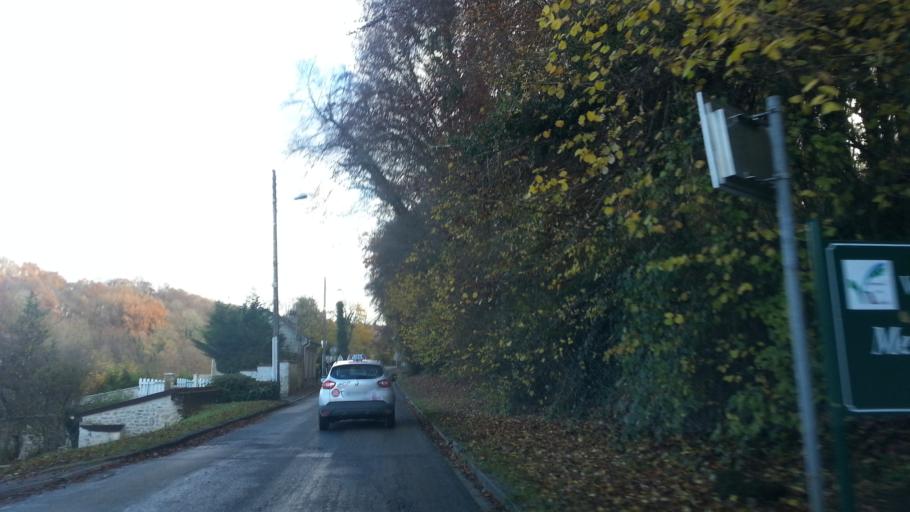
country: FR
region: Picardie
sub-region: Departement de l'Oise
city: Verneuil-en-Halatte
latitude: 49.2647
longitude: 2.5355
